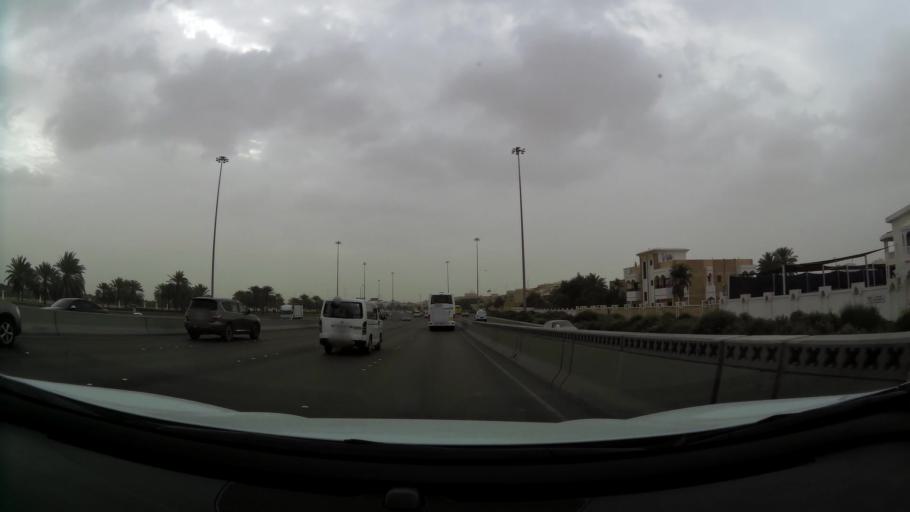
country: AE
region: Abu Dhabi
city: Abu Dhabi
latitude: 24.4523
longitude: 54.4047
